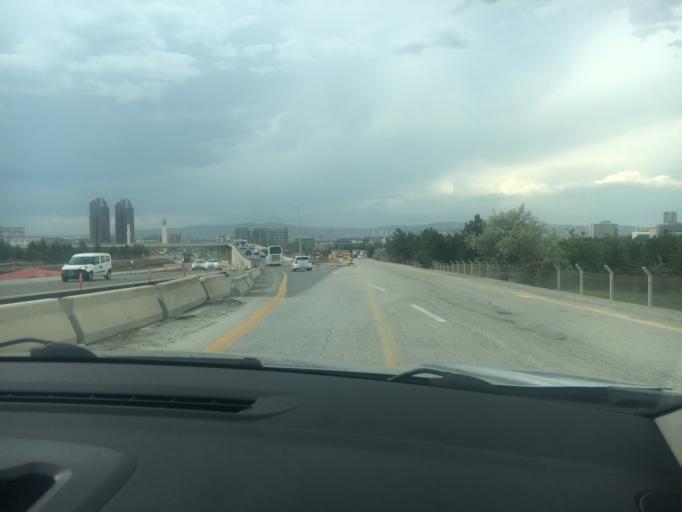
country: TR
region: Ankara
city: Batikent
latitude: 39.8974
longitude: 32.7668
